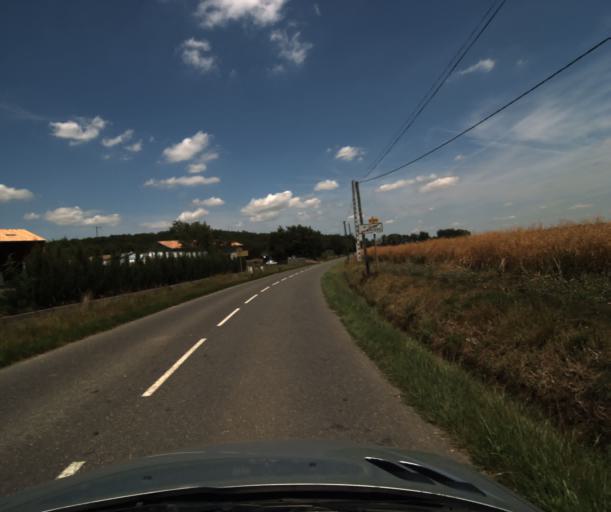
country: FR
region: Midi-Pyrenees
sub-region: Departement de la Haute-Garonne
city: Labastidette
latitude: 43.4753
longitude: 1.2157
